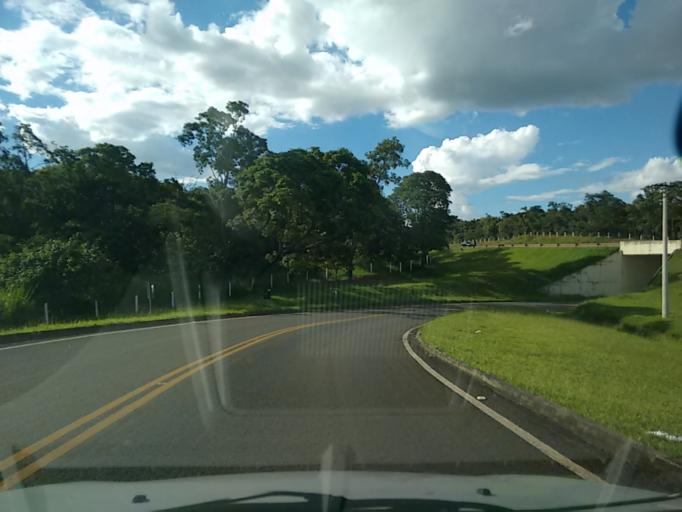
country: BR
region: Sao Paulo
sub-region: Sao Carlos
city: Sao Carlos
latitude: -22.0742
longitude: -47.8440
